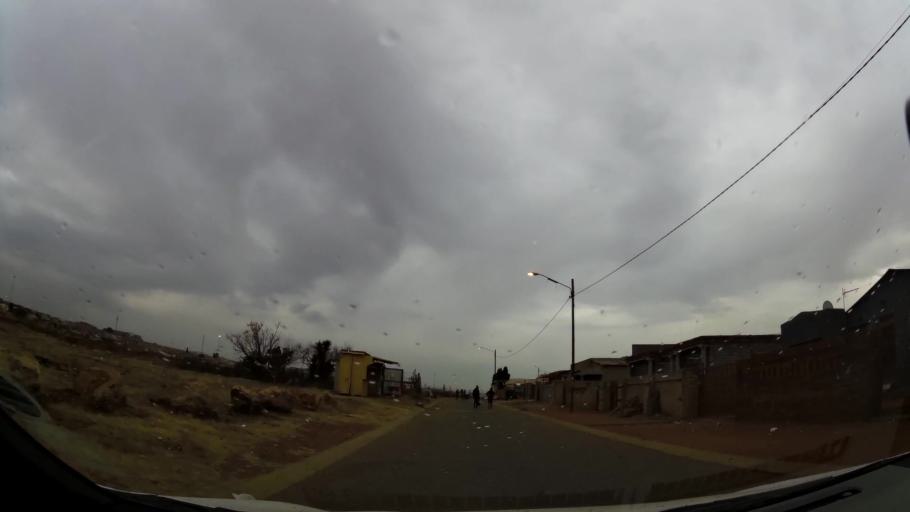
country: ZA
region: Gauteng
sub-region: Ekurhuleni Metropolitan Municipality
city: Germiston
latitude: -26.3775
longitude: 28.1722
